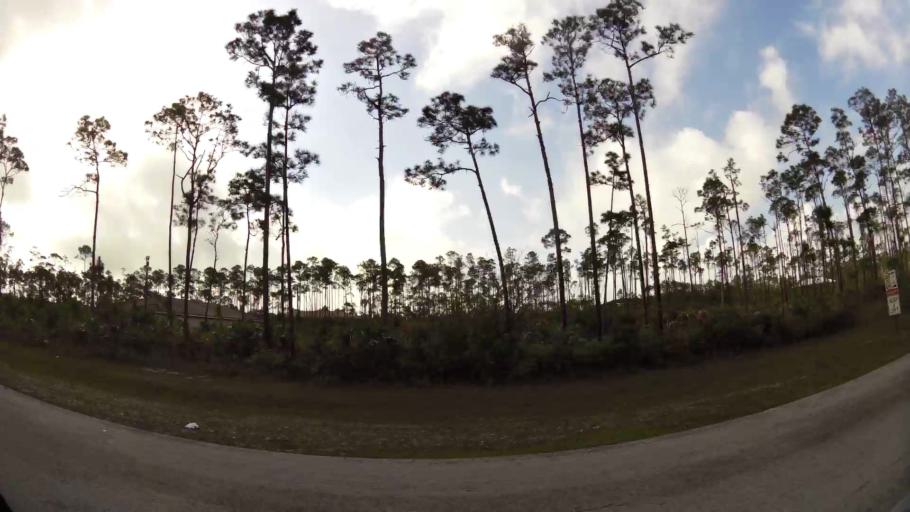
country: BS
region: Freeport
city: Lucaya
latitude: 26.5680
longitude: -78.5830
